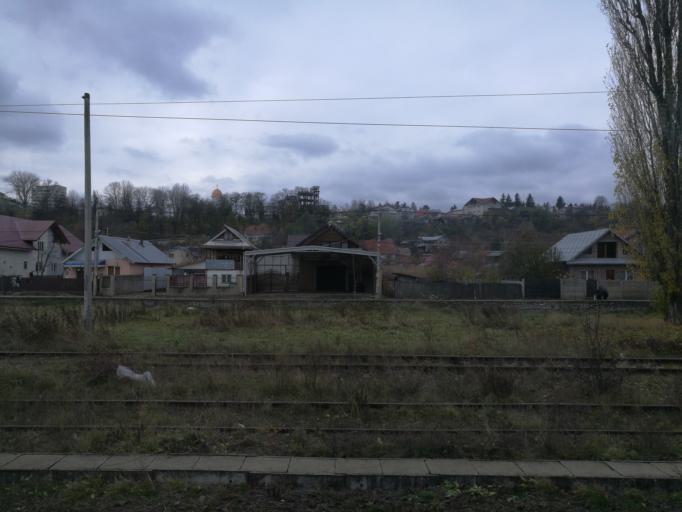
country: RO
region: Iasi
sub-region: Municipiul Pascani
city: Pascani
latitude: 47.2484
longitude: 26.7292
